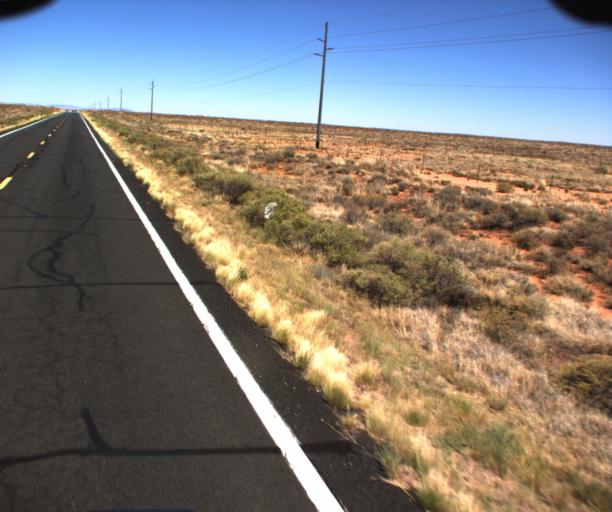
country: US
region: Arizona
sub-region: Coconino County
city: LeChee
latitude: 34.8965
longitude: -110.8594
